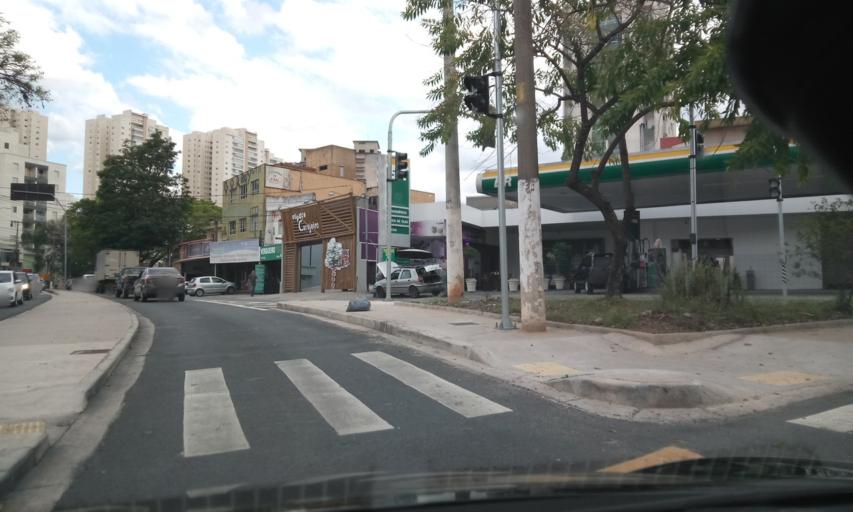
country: BR
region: Sao Paulo
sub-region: Sao Bernardo Do Campo
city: Sao Bernardo do Campo
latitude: -23.6853
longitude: -46.5550
